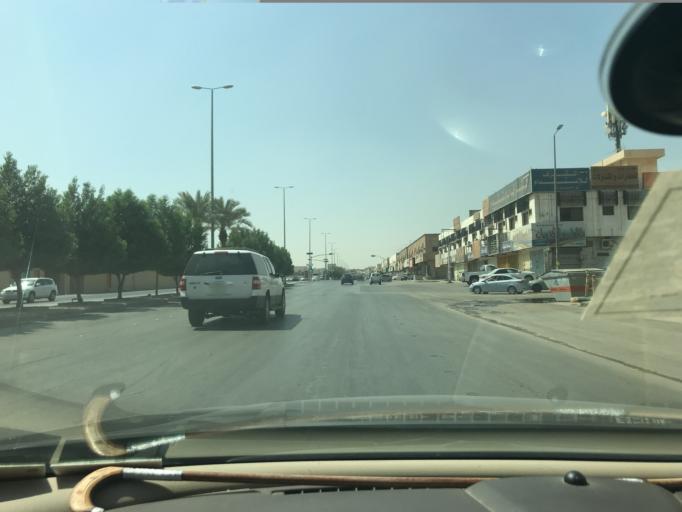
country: SA
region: Ar Riyad
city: Riyadh
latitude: 24.7075
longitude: 46.7865
